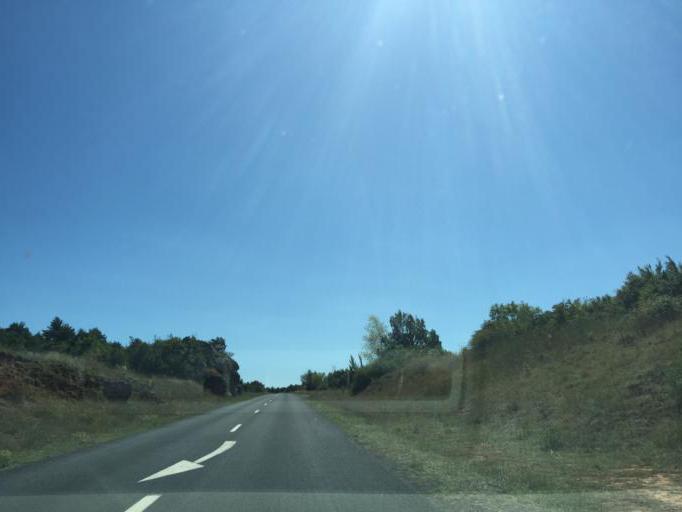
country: FR
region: Midi-Pyrenees
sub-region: Departement de l'Aveyron
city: La Cavalerie
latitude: 43.9072
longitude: 3.3107
